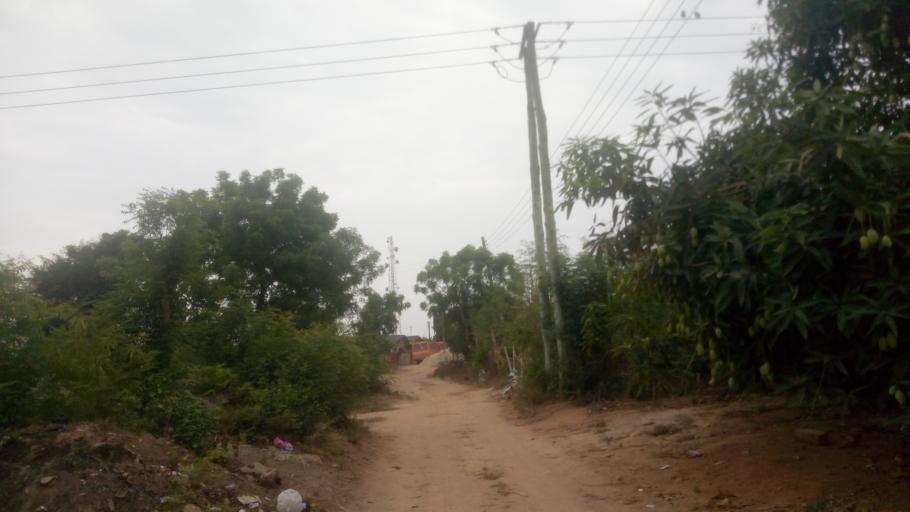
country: GH
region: Central
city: Winneba
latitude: 5.3619
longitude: -0.6283
